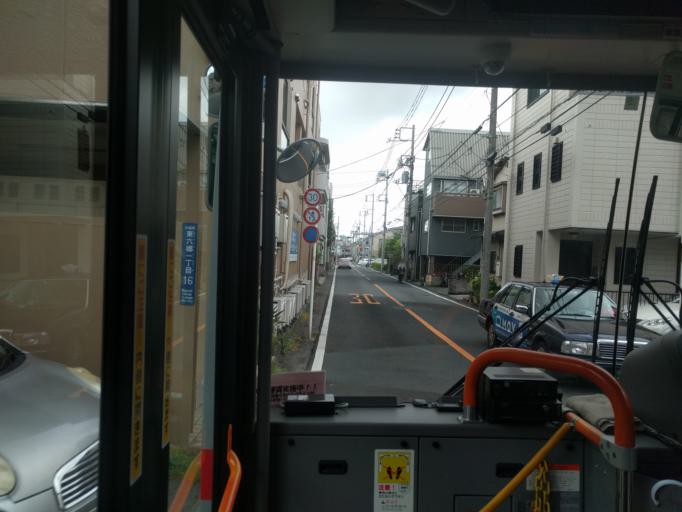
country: JP
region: Kanagawa
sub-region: Kawasaki-shi
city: Kawasaki
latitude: 35.5520
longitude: 139.7210
